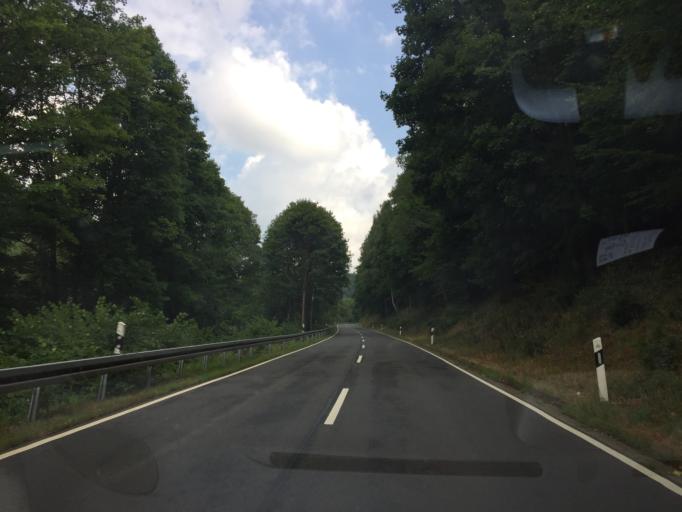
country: DE
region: Lower Saxony
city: Zorge
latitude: 51.6448
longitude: 10.6440
